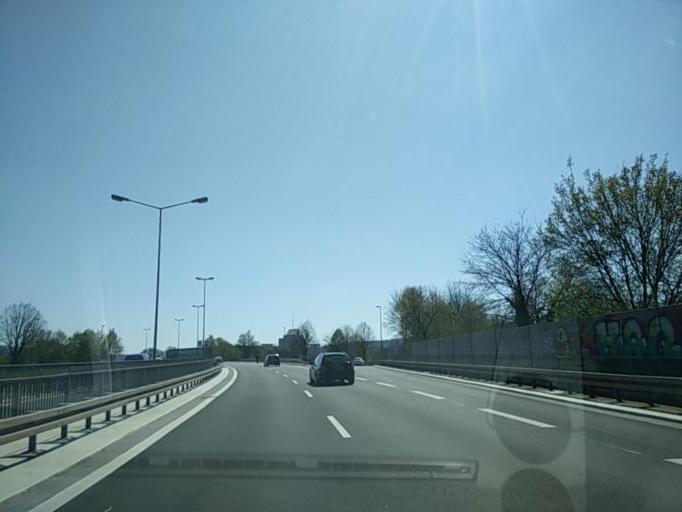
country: DE
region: Baden-Wuerttemberg
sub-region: Tuebingen Region
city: Tuebingen
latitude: 48.5155
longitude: 9.0457
